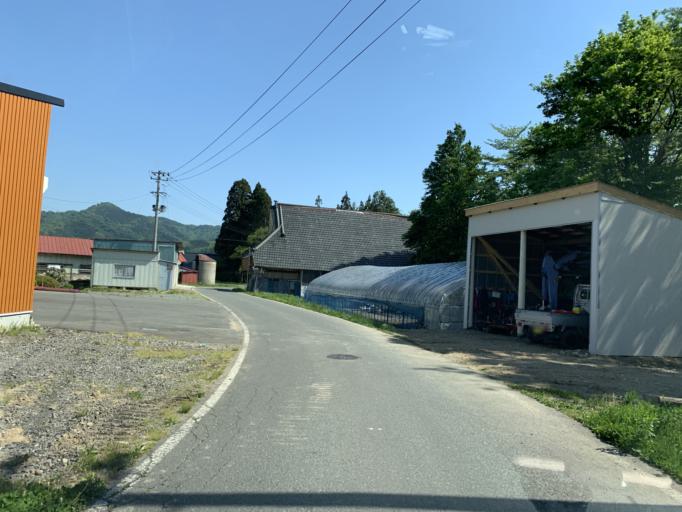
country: JP
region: Iwate
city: Shizukuishi
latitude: 39.5589
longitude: 140.8414
